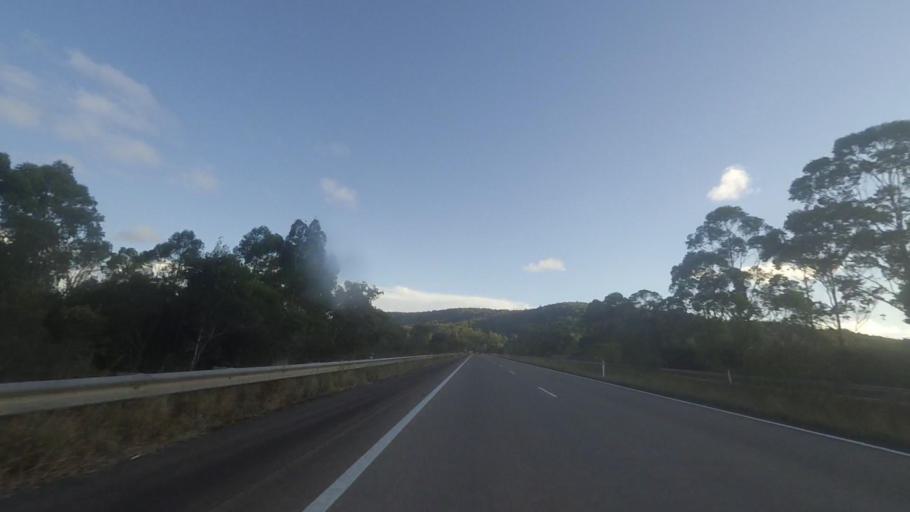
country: AU
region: New South Wales
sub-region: Great Lakes
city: Nabiac
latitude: -32.2676
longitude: 152.3283
